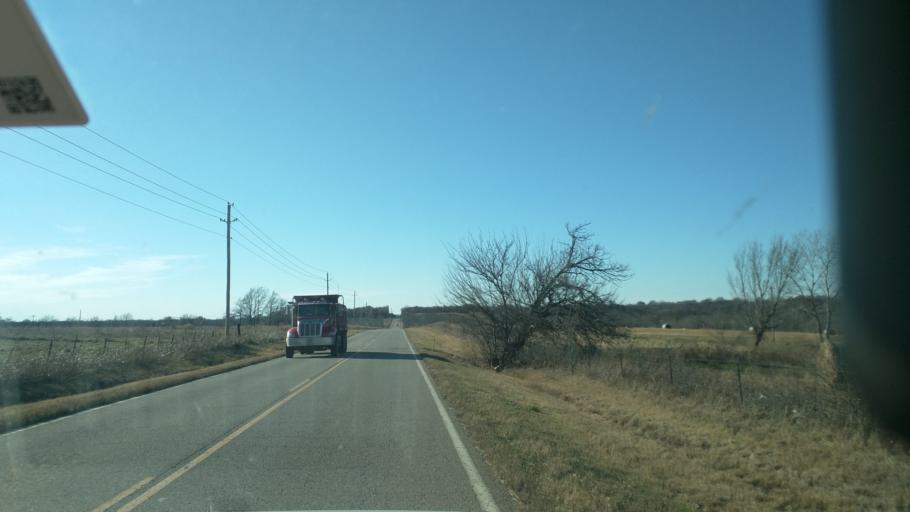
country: US
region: Oklahoma
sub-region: Nowata County
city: Nowata
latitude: 36.7717
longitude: -95.5614
